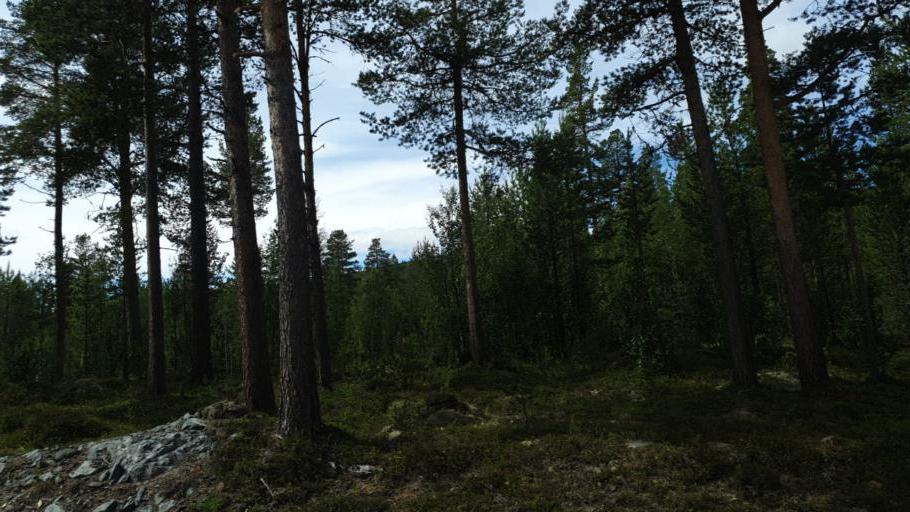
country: NO
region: Oppland
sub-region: Vaga
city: Vagamo
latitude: 61.6947
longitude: 9.0606
